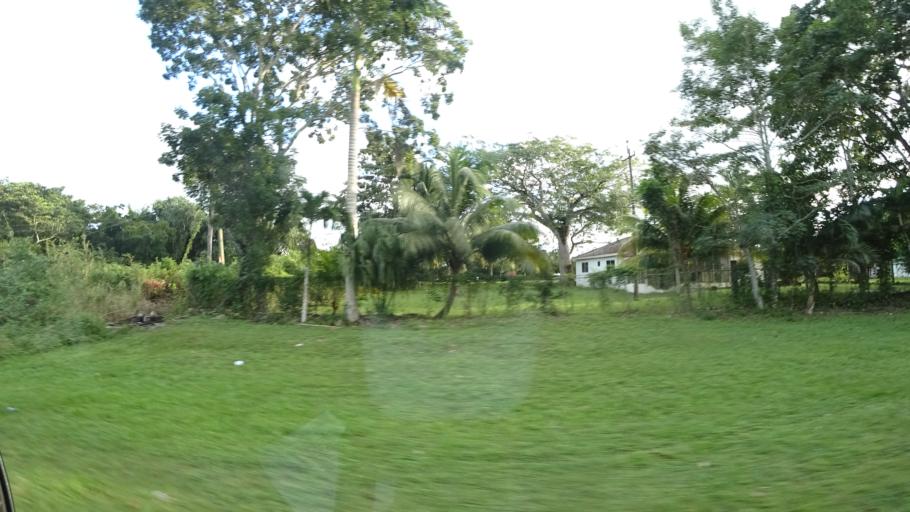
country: BZ
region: Belize
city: Belize City
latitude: 17.5715
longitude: -88.3939
